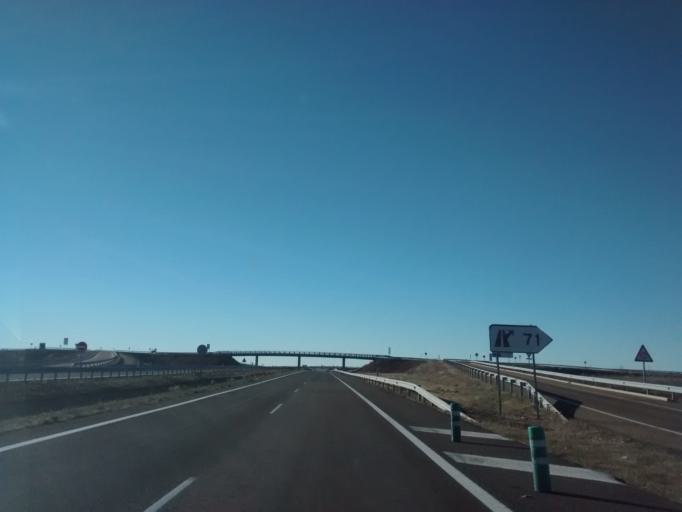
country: ES
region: Castille and Leon
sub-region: Provincia de Palencia
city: Santa Cruz de Boedo
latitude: 42.5424
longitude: -4.3786
